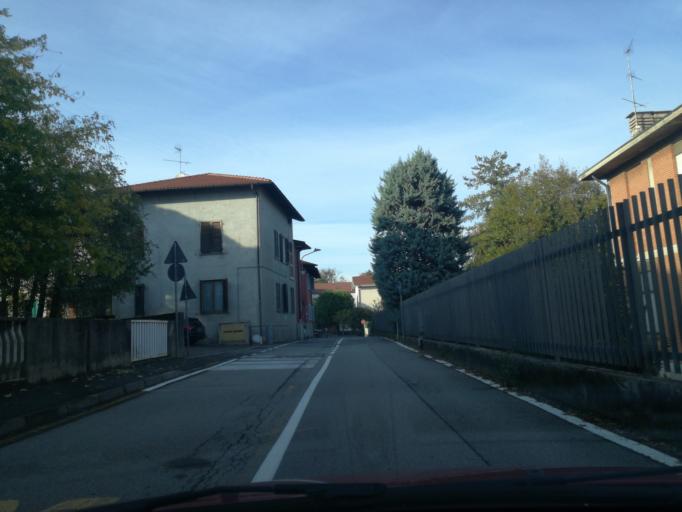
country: IT
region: Lombardy
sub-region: Provincia di Monza e Brianza
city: Villanova
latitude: 45.6391
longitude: 9.3942
